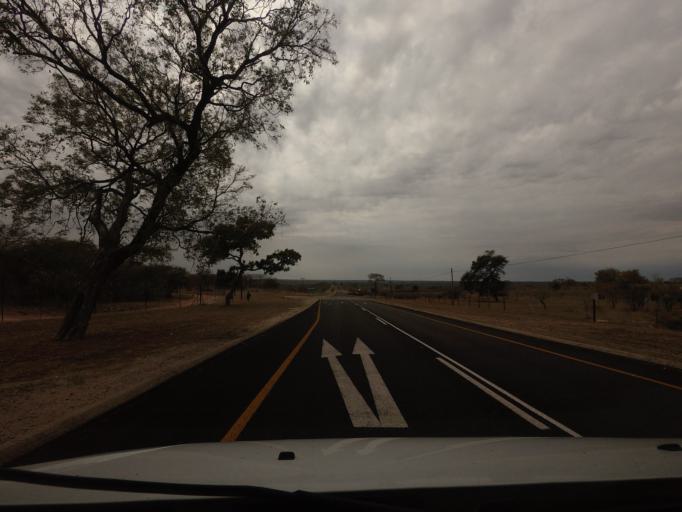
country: ZA
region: Limpopo
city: Thulamahashi
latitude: -24.5614
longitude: 31.1575
